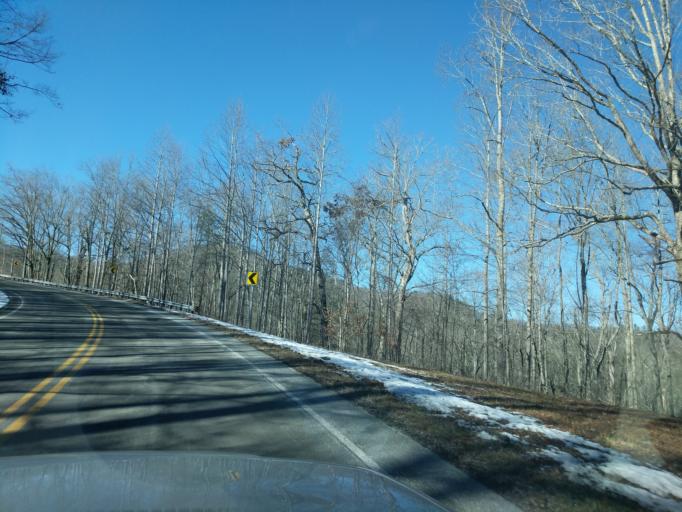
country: US
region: Georgia
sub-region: Rabun County
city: Clayton
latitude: 34.8749
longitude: -83.5669
